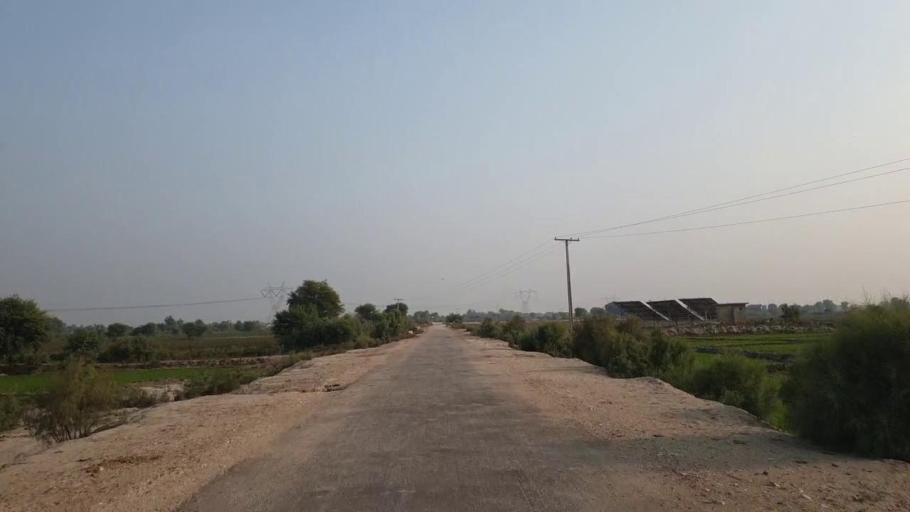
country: PK
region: Sindh
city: Bhan
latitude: 26.4962
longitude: 67.7684
